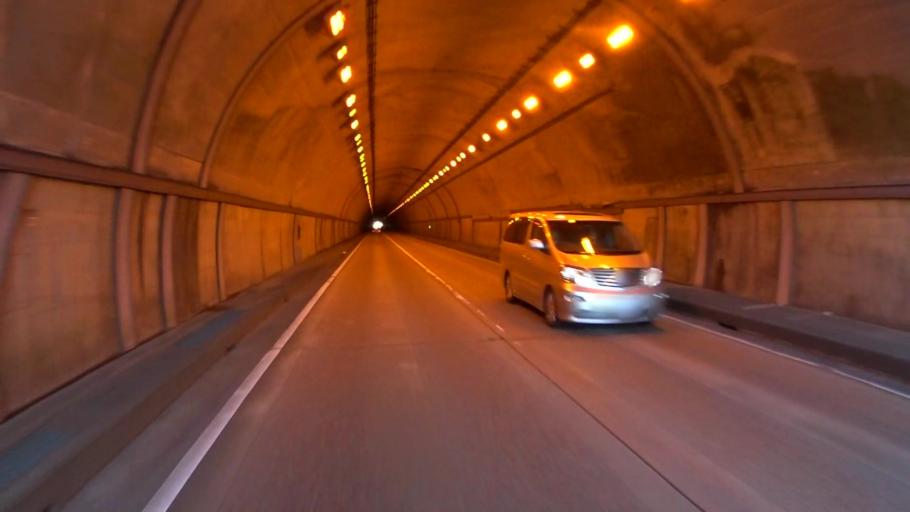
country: JP
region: Kyoto
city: Fukuchiyama
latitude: 35.4136
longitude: 135.0865
